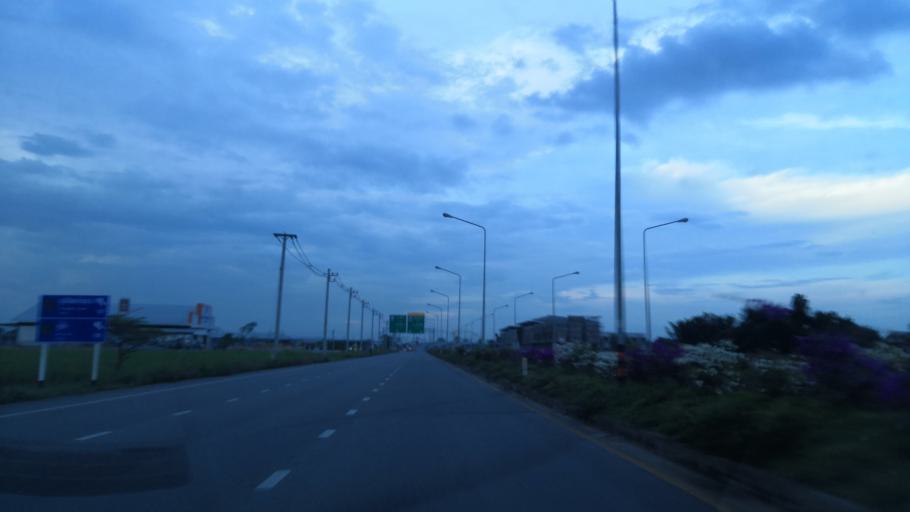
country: TH
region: Chiang Rai
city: Chiang Rai
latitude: 19.8558
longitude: 99.8365
